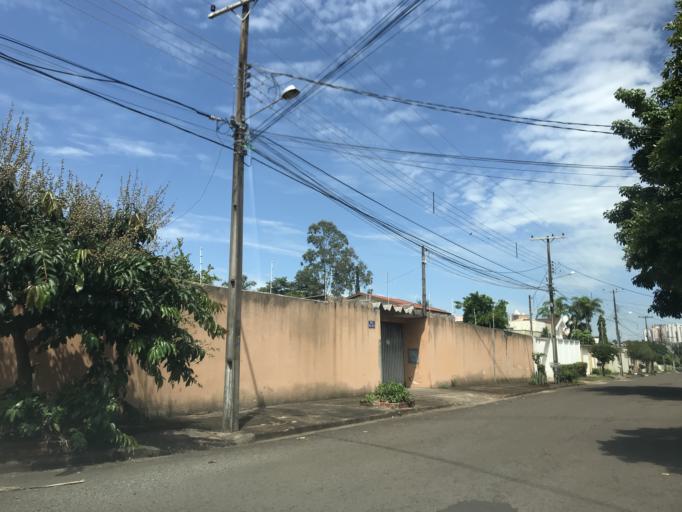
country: BR
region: Parana
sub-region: Londrina
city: Londrina
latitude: -23.3484
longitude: -51.1611
